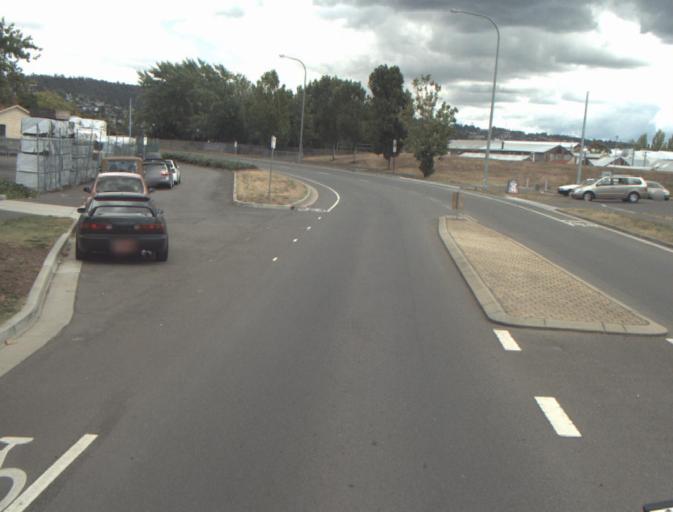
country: AU
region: Tasmania
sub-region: Launceston
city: East Launceston
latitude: -41.4287
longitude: 147.1451
